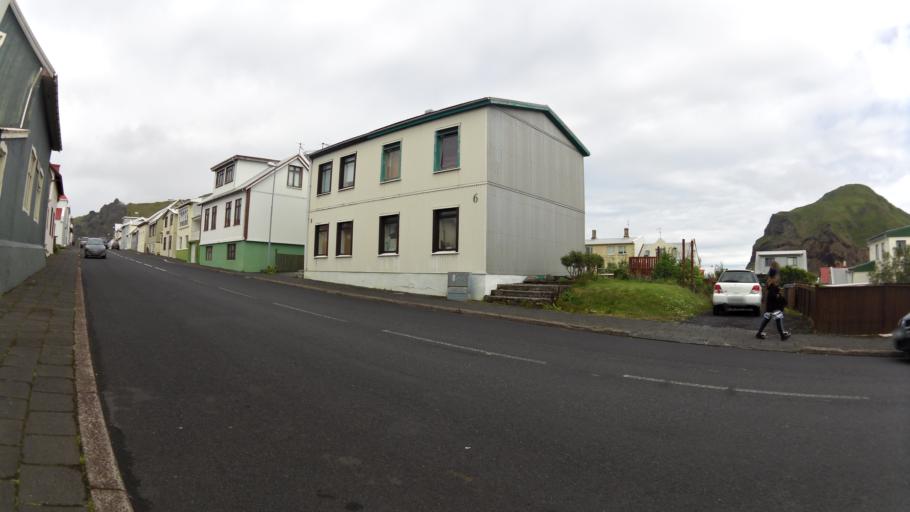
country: IS
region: South
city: Vestmannaeyjar
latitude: 63.4385
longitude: -20.2718
